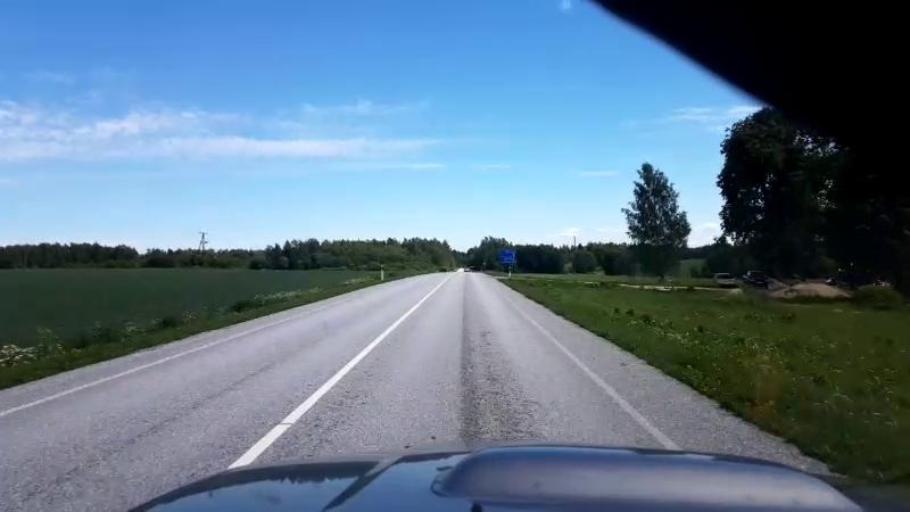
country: EE
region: Laeaene-Virumaa
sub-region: Rakke vald
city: Rakke
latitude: 58.9176
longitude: 26.2549
